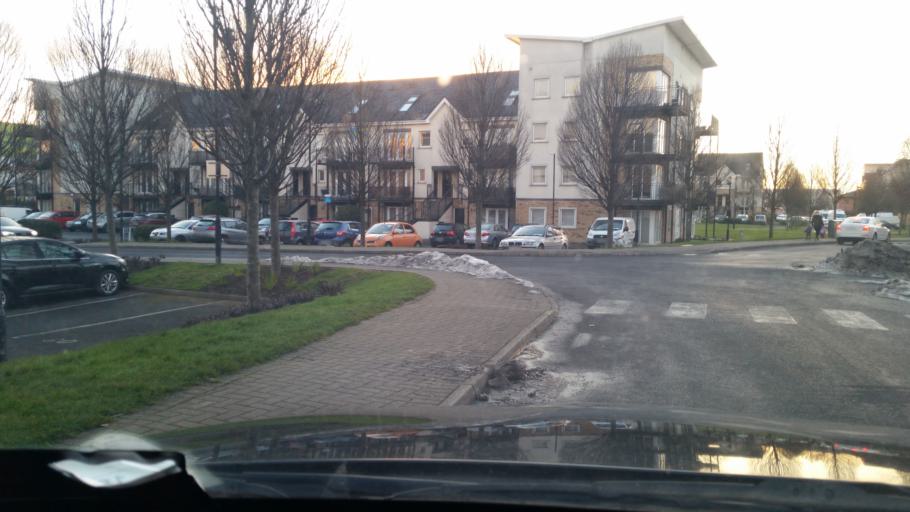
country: IE
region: Leinster
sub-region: Dublin City
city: Finglas
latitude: 53.4008
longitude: -6.2934
